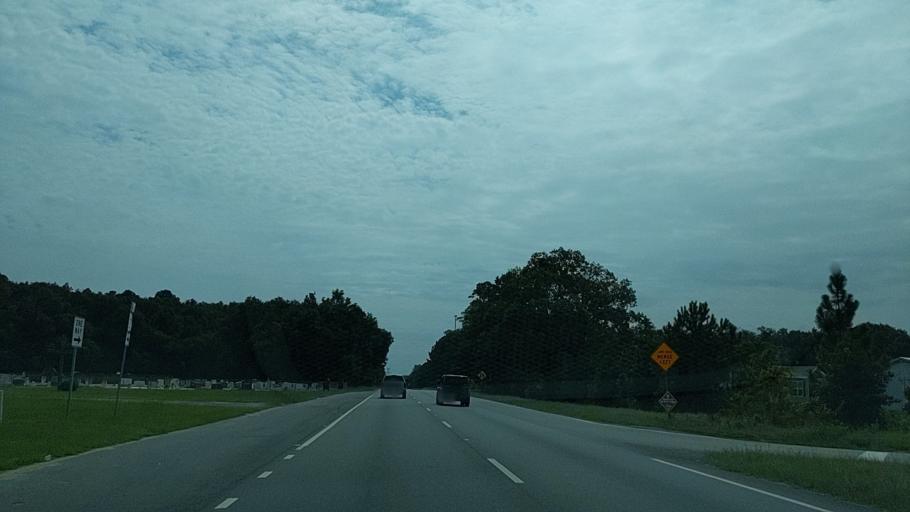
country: US
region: Georgia
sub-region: Effingham County
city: Rincon
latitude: 32.2504
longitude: -81.2124
